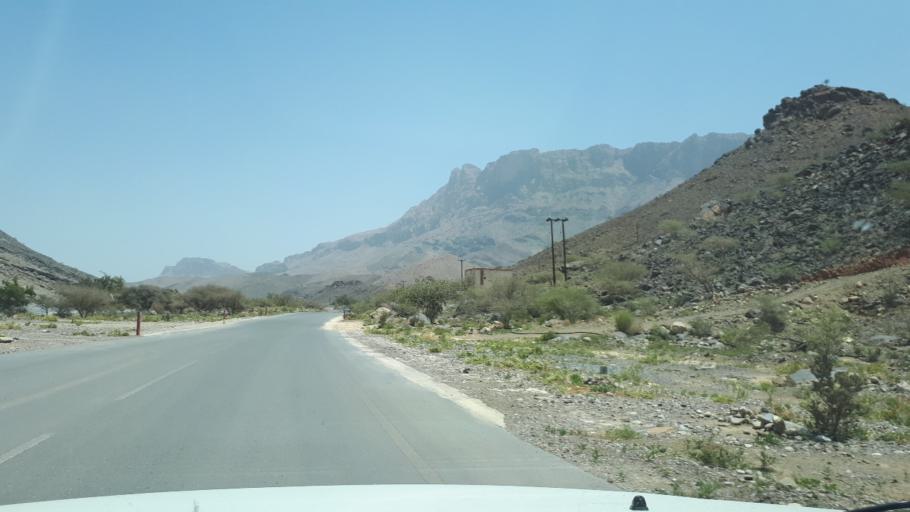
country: OM
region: Muhafazat ad Dakhiliyah
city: Bahla'
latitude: 23.1696
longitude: 57.1562
